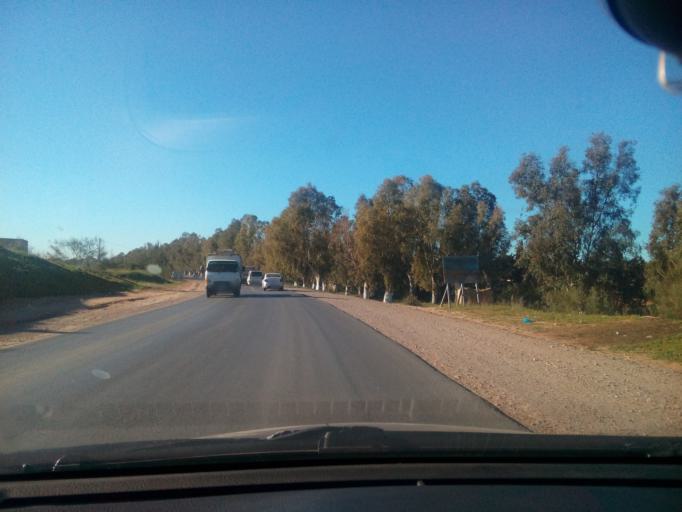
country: DZ
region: Mostaganem
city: Mostaganem
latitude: 35.9036
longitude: 0.2105
